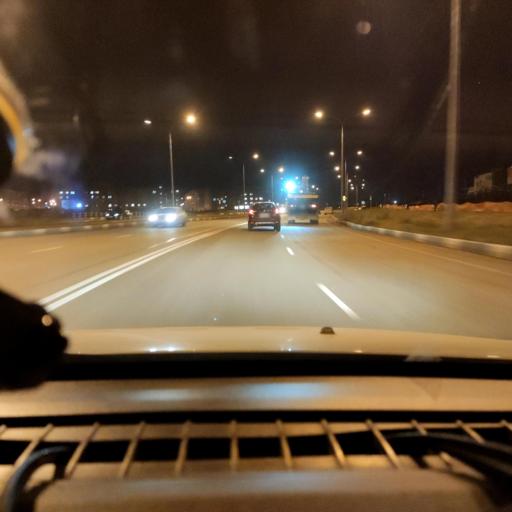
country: RU
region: Samara
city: Samara
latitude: 53.1415
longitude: 50.0780
